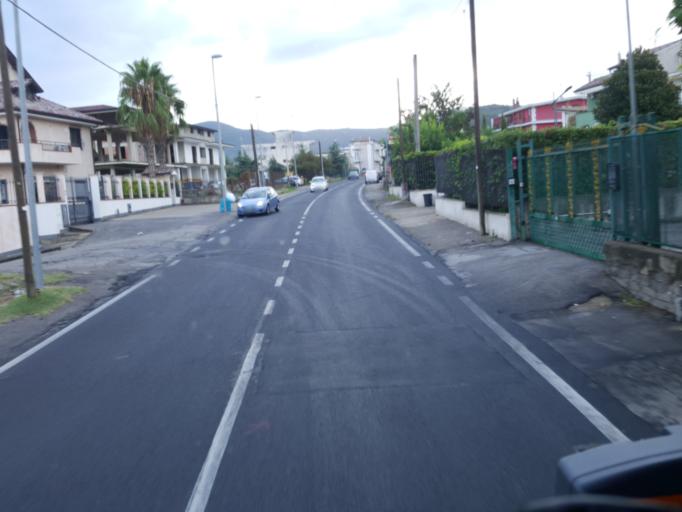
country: IT
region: Campania
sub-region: Provincia di Napoli
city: Carbonara di Nola
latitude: 40.8797
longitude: 14.5648
